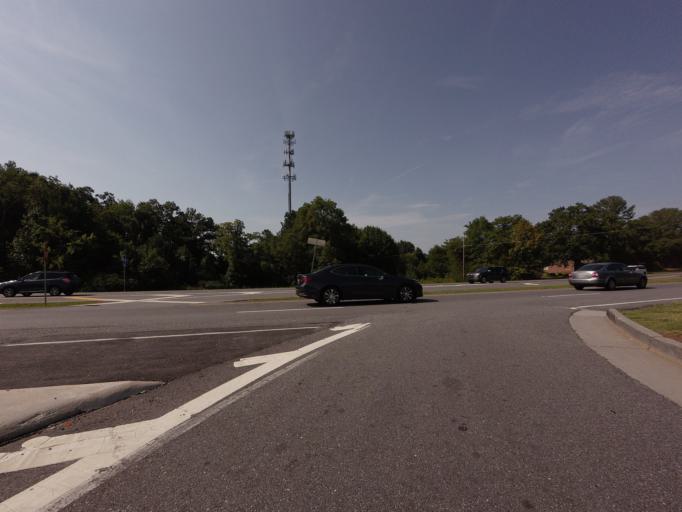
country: US
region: Georgia
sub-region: Fulton County
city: Johns Creek
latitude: 34.0650
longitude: -84.2150
